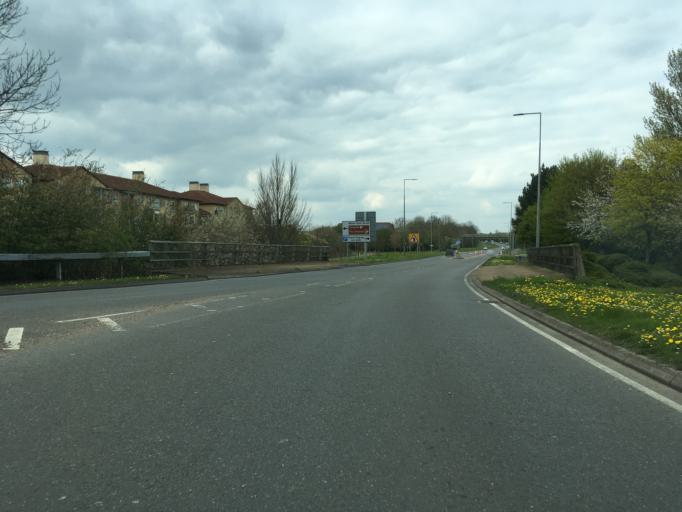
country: GB
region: England
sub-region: Milton Keynes
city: Milton Keynes
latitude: 52.0549
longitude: -0.7281
